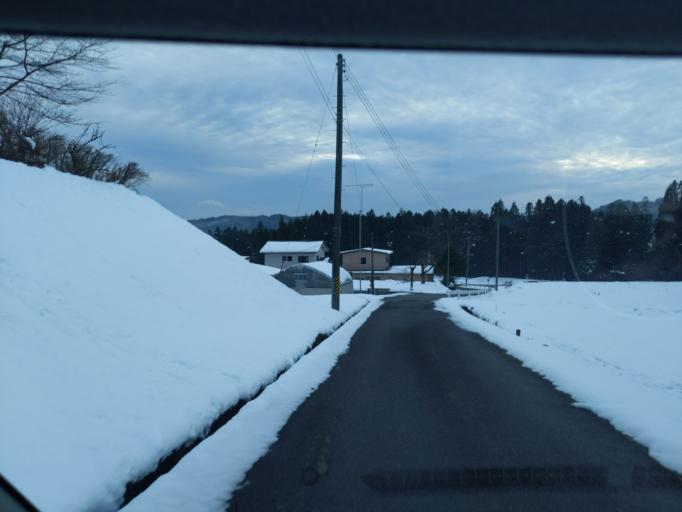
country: JP
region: Iwate
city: Mizusawa
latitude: 39.0492
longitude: 141.0575
